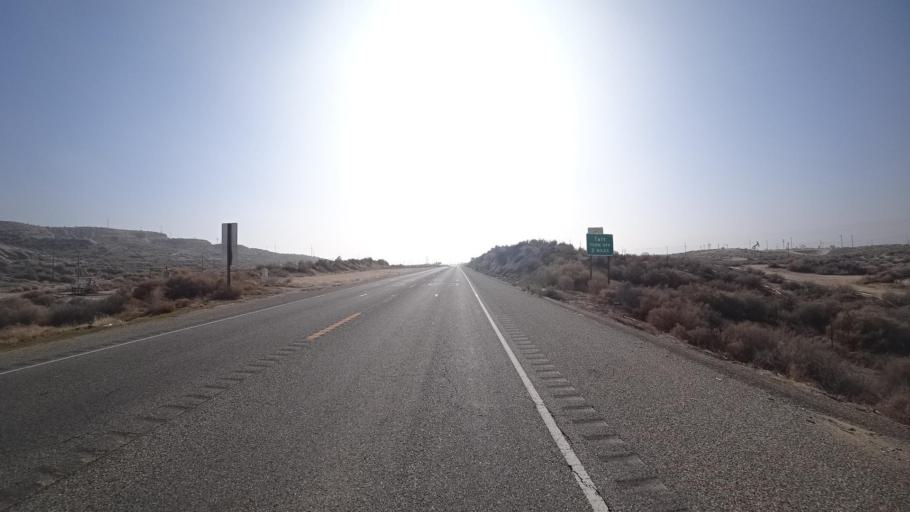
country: US
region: California
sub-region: Kern County
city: Ford City
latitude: 35.1696
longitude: -119.4536
